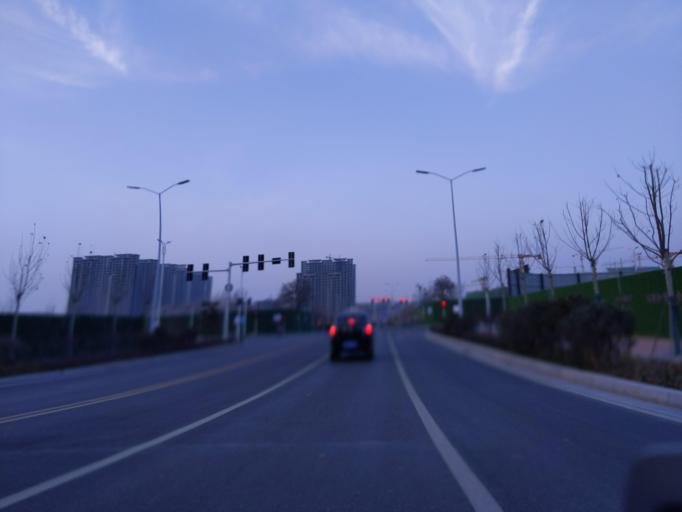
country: CN
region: Henan Sheng
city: Puyang
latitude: 35.8097
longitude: 115.0114
